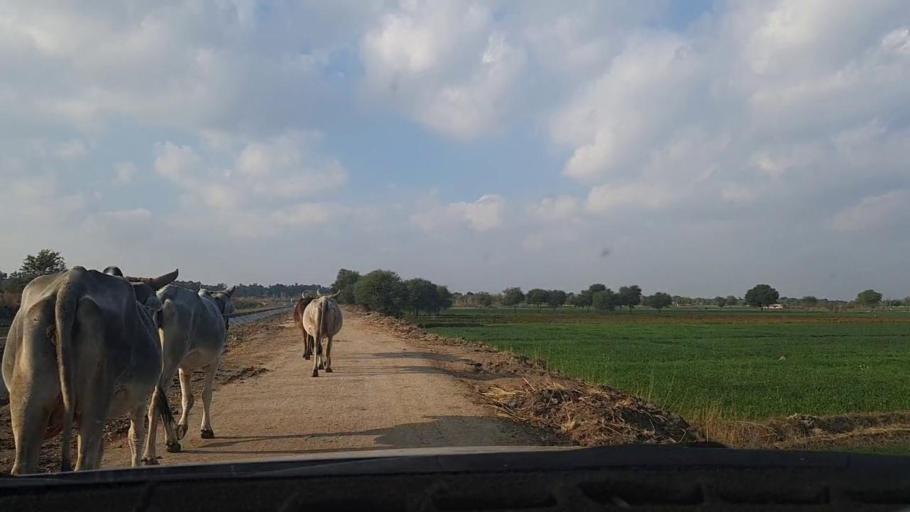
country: PK
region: Sindh
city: Tando Mittha Khan
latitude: 25.9085
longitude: 69.3084
